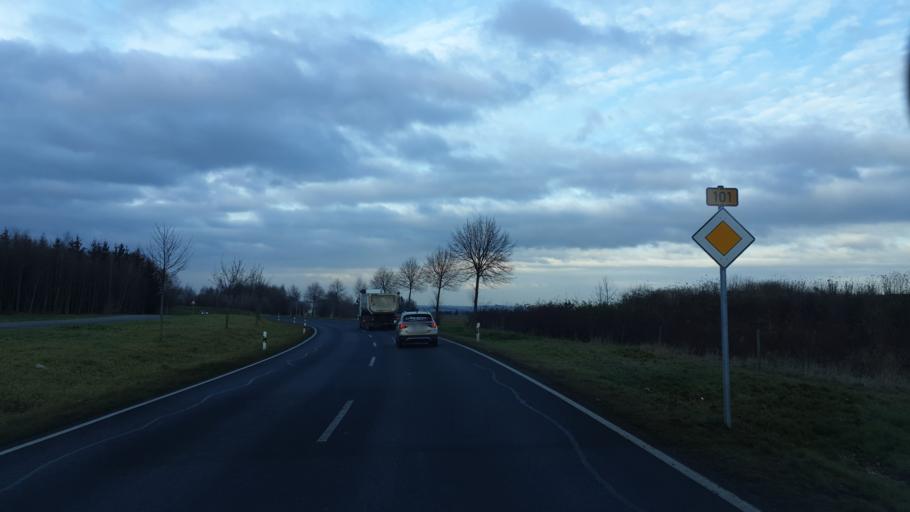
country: DE
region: Saxony
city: Nossen
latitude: 51.0174
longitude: 13.3047
